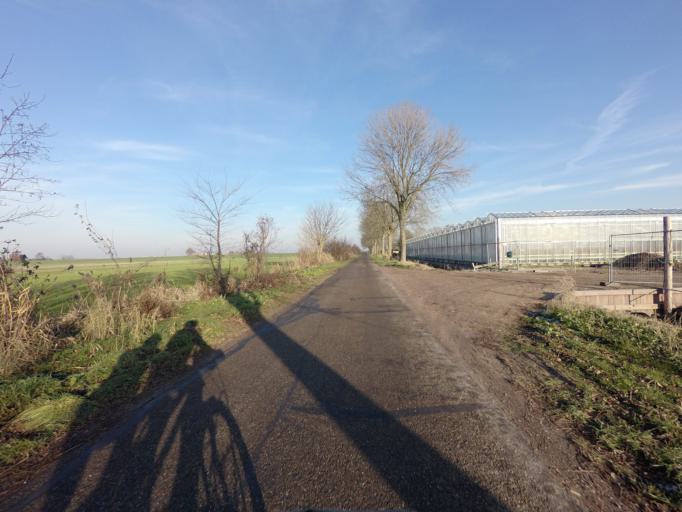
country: NL
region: Utrecht
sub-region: Gemeente De Ronde Venen
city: Mijdrecht
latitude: 52.2099
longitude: 4.8418
